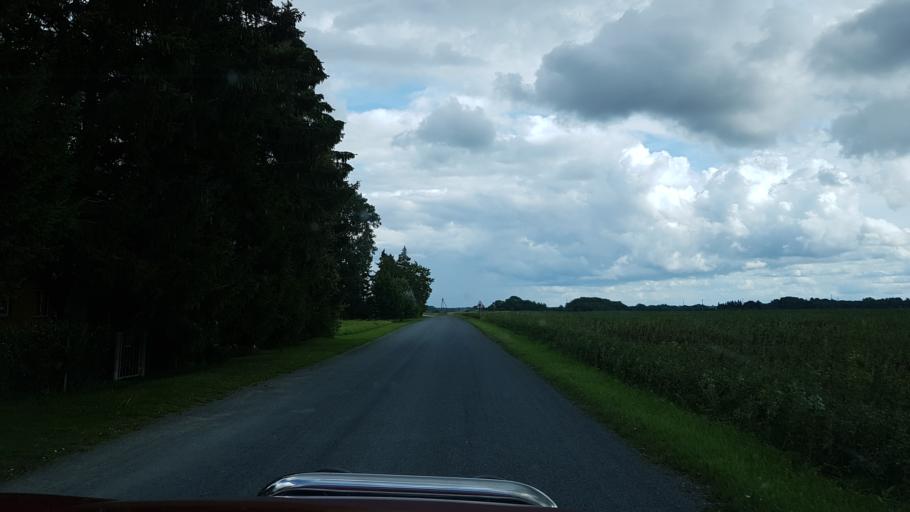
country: EE
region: Laeaene
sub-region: Lihula vald
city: Lihula
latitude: 58.7087
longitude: 24.0350
